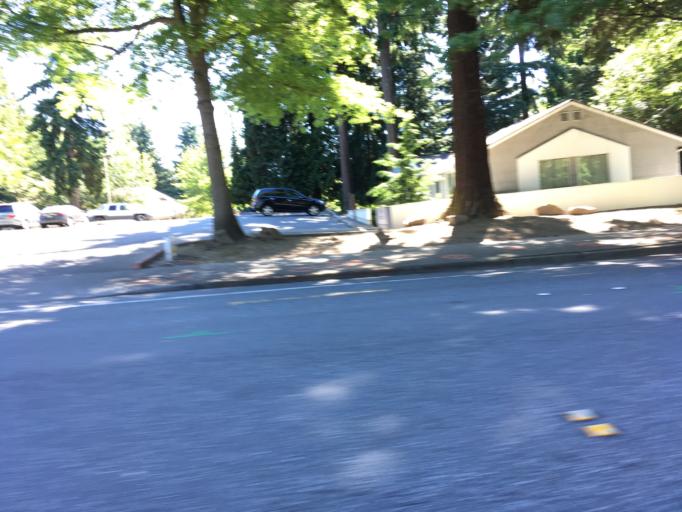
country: US
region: Washington
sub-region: King County
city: Bellevue
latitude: 47.6233
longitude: -122.1911
